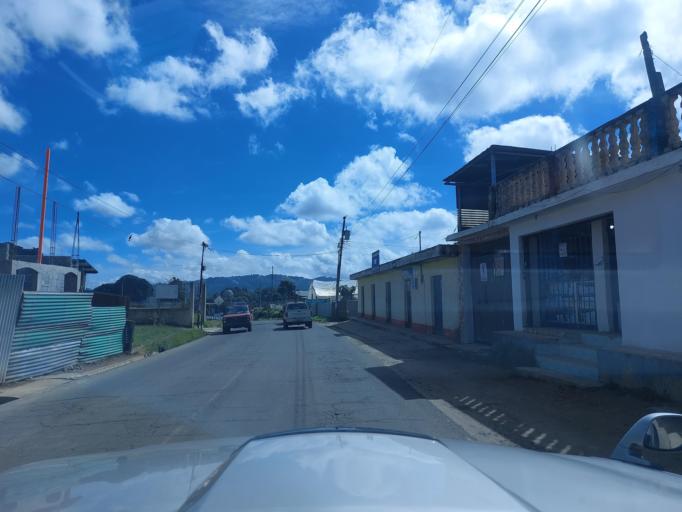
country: GT
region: Chimaltenango
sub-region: Municipio de Zaragoza
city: Zaragoza
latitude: 14.6732
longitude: -90.8984
